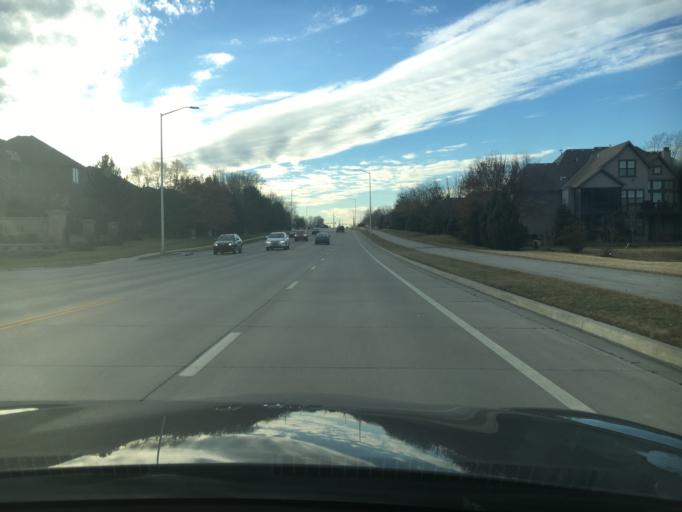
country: US
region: Kansas
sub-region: Johnson County
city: Leawood
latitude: 38.8693
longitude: -94.6425
